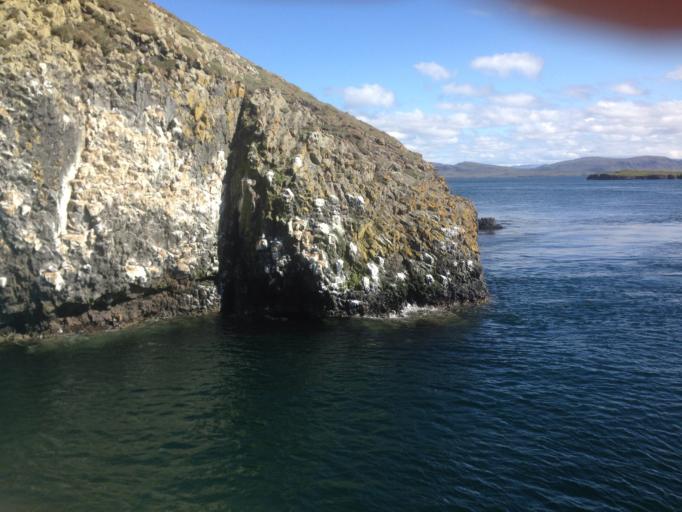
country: IS
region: West
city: Stykkisholmur
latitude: 65.0840
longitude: -22.6803
